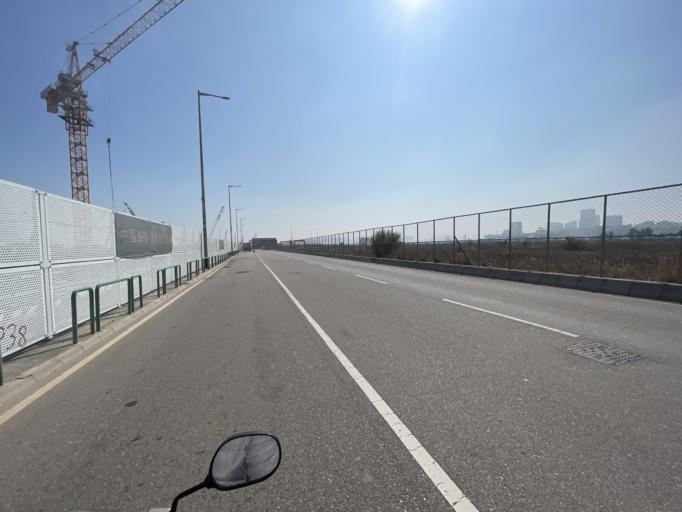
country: MO
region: Macau
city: Macau
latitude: 22.2054
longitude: 113.5649
